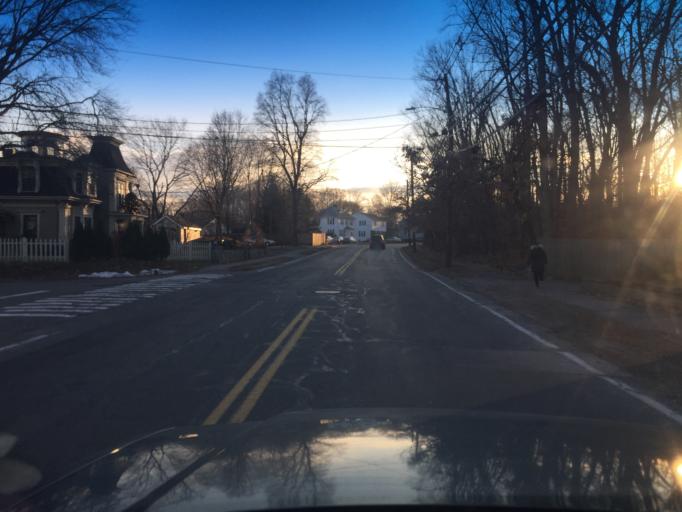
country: US
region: Massachusetts
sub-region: Norfolk County
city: Norwood
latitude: 42.1960
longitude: -71.1887
